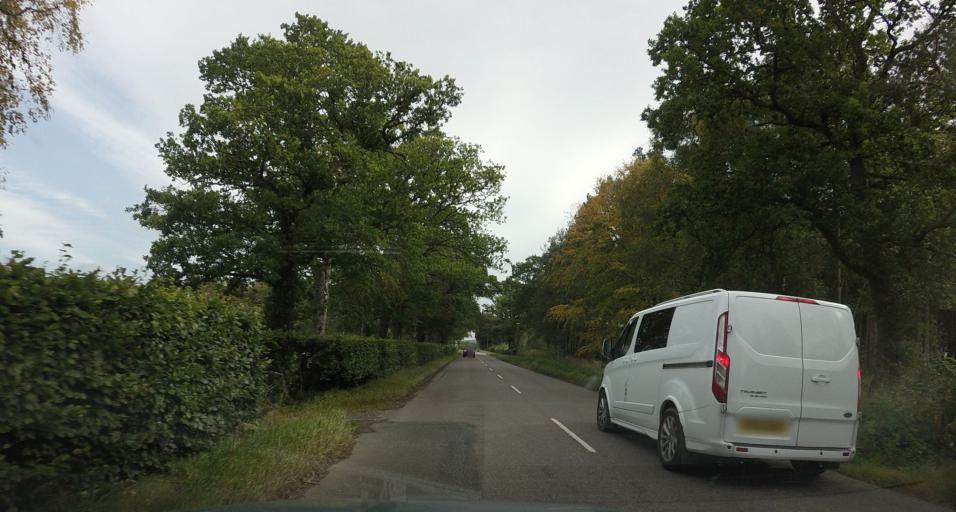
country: GB
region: Scotland
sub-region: Aberdeenshire
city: Kemnay
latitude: 57.2243
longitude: -2.5175
